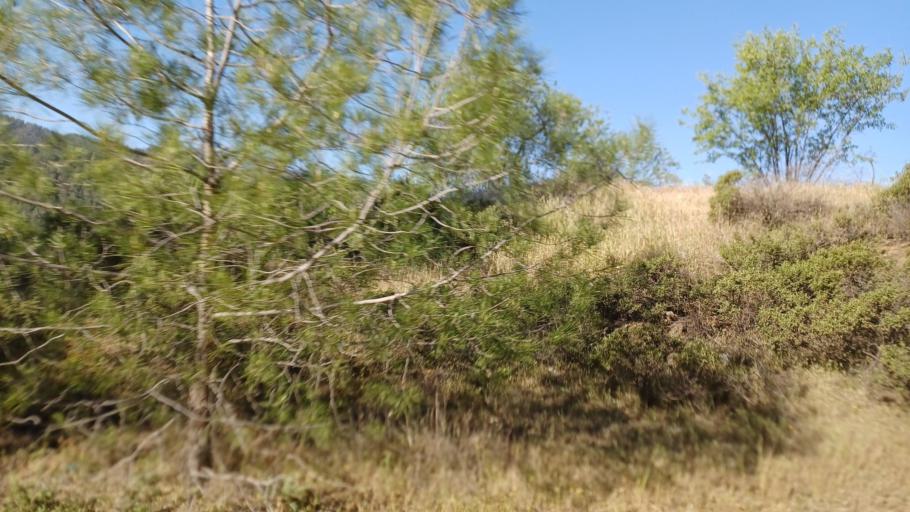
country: CY
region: Lefkosia
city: Peristerona
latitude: 35.0259
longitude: 33.0545
